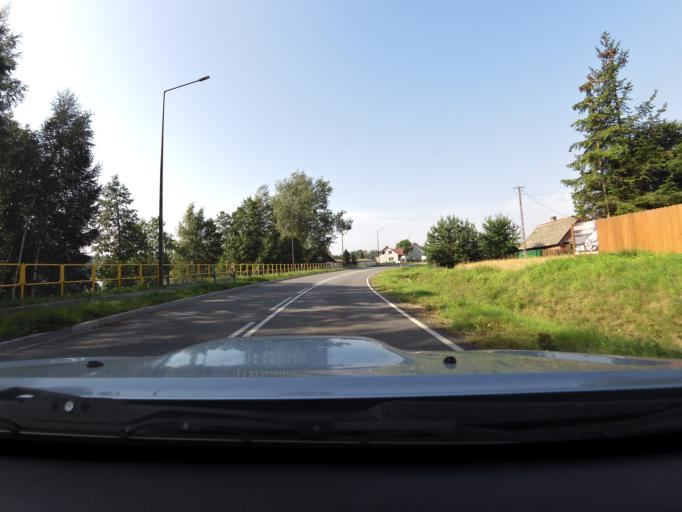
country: PL
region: Podlasie
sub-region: Powiat sejnenski
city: Krasnopol
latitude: 54.0824
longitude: 23.1205
